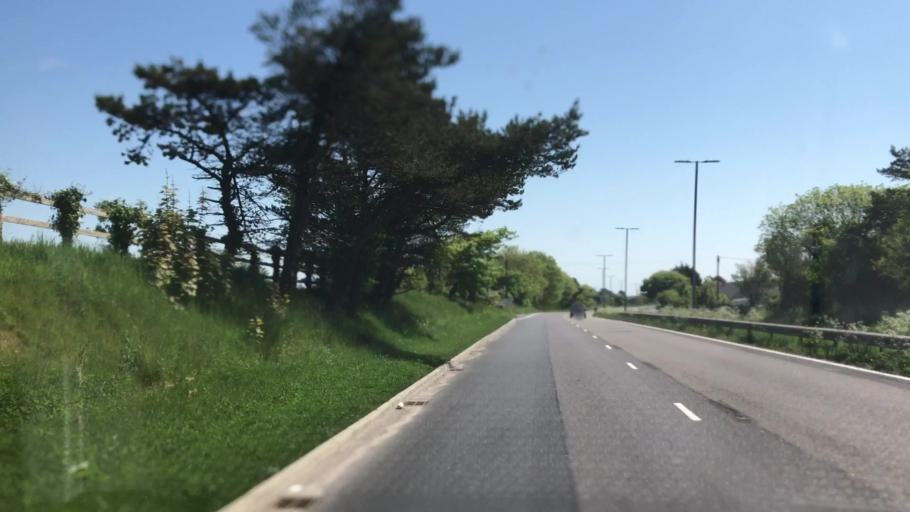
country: GB
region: England
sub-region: Cornwall
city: Chacewater
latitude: 50.2644
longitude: -5.1158
